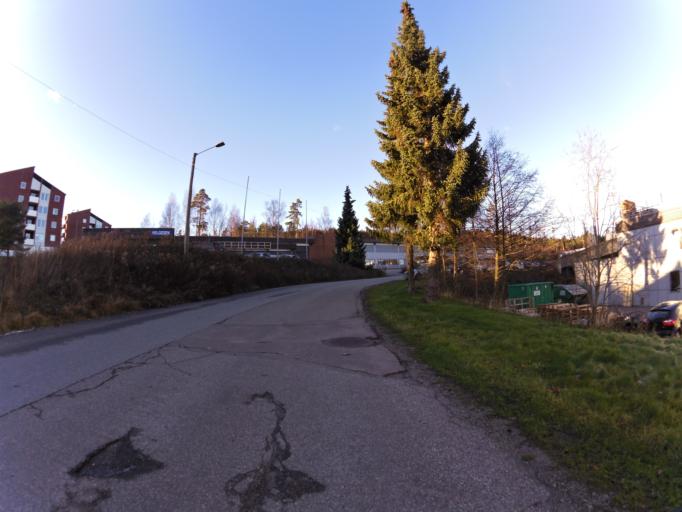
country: NO
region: Ostfold
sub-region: Fredrikstad
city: Fredrikstad
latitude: 59.2363
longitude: 10.9644
